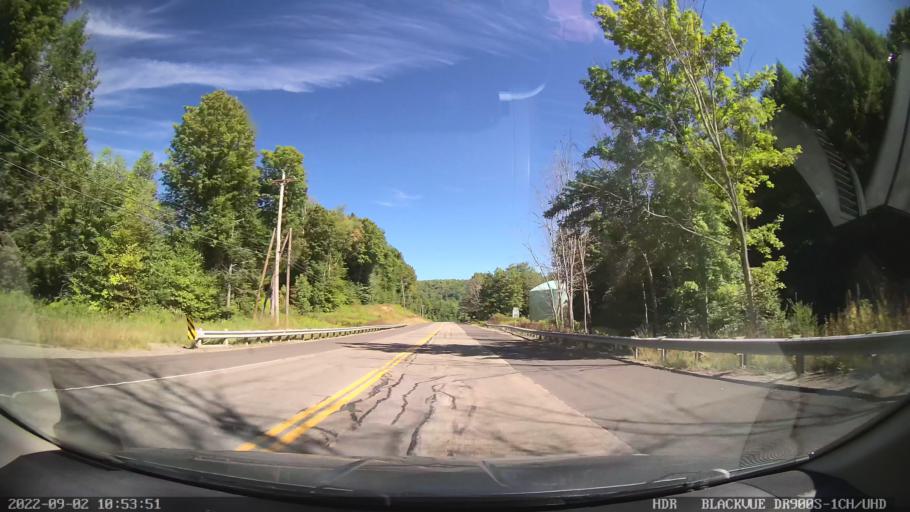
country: US
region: Pennsylvania
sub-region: Tioga County
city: Blossburg
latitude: 41.6517
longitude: -77.0952
